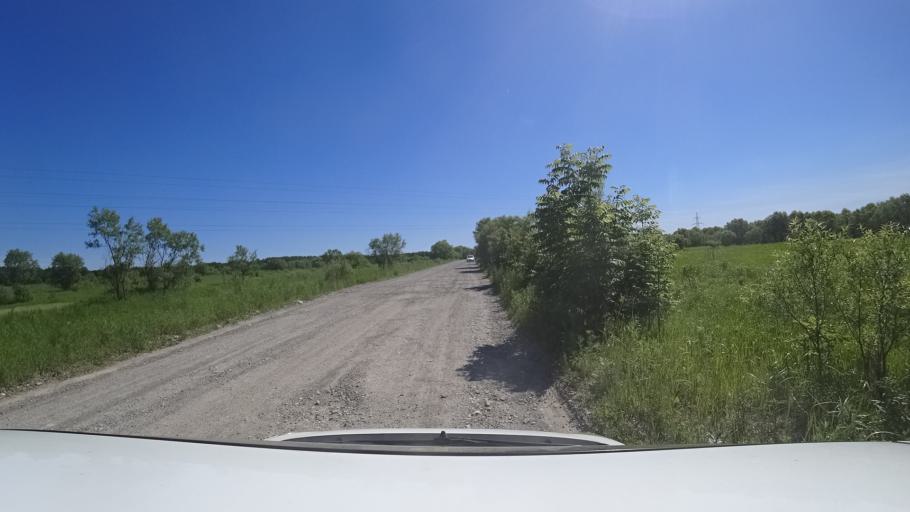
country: RU
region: Khabarovsk Krai
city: Topolevo
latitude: 48.5642
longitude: 135.1970
